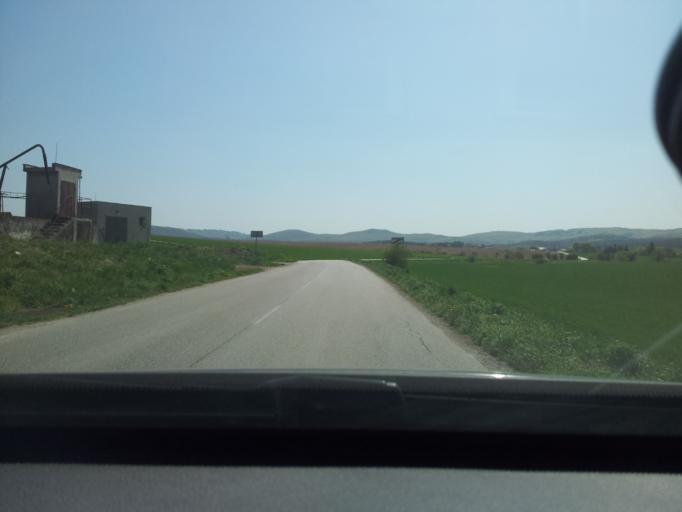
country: SK
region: Nitriansky
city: Partizanske
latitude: 48.5592
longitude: 18.3272
